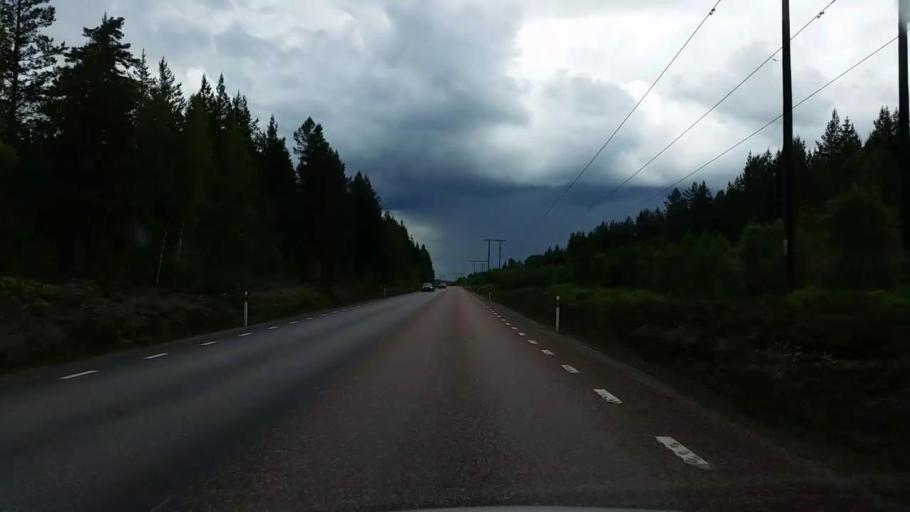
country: SE
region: Gaevleborg
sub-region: Hofors Kommun
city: Hofors
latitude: 60.5260
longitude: 16.4524
